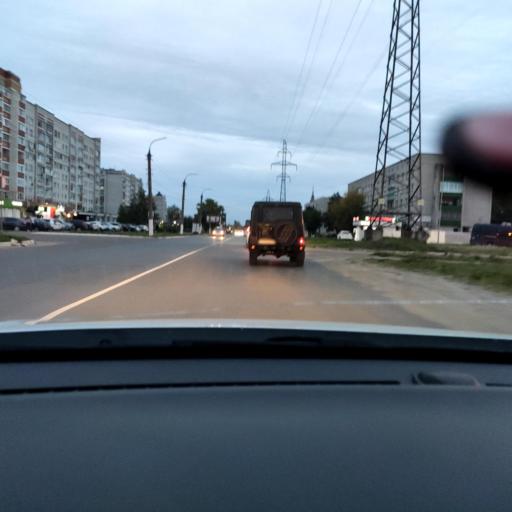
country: RU
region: Mariy-El
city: Volzhsk
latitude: 55.8675
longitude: 48.3508
